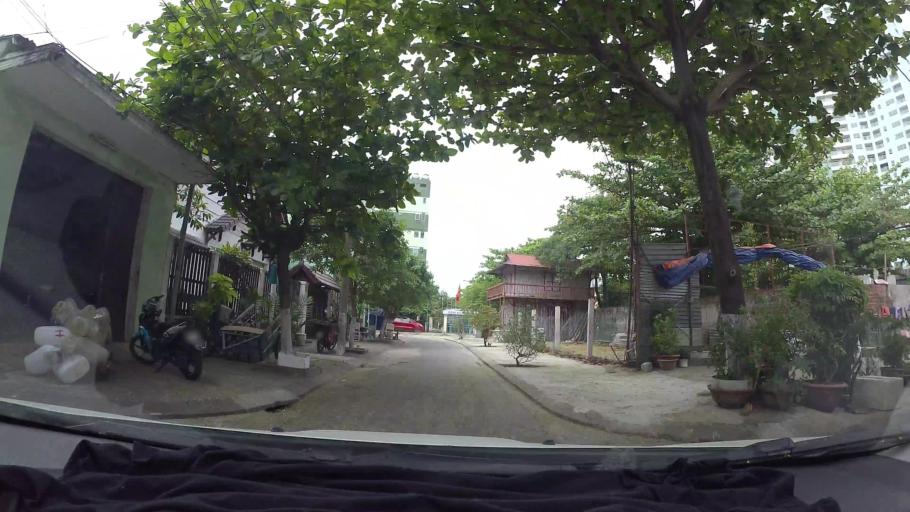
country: VN
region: Da Nang
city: Da Nang
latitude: 16.0895
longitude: 108.2165
